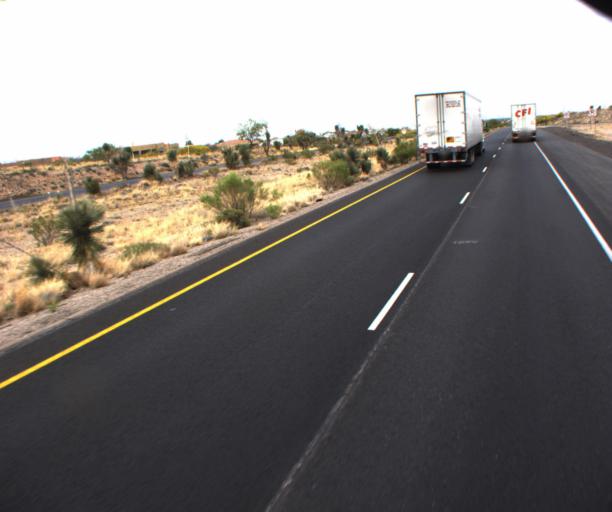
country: US
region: Arizona
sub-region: Pima County
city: Vail
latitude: 32.0092
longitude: -110.6933
